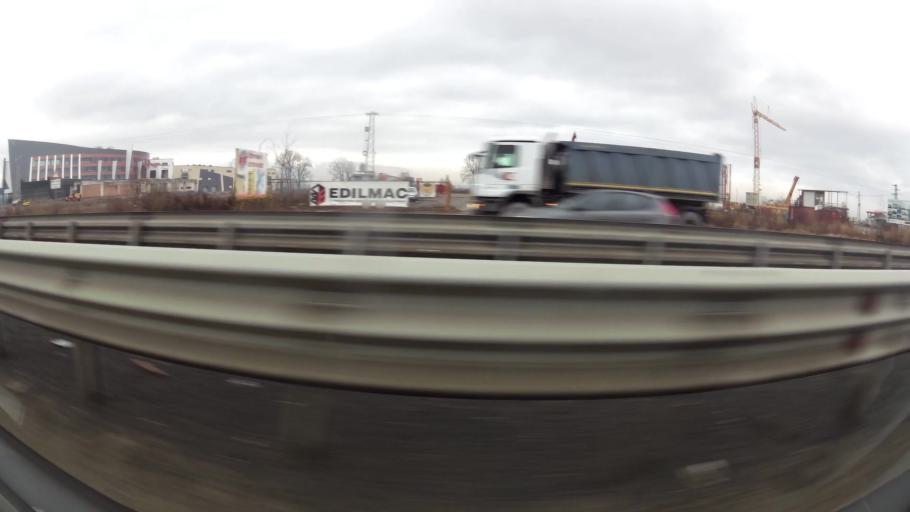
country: BG
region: Sofia-Capital
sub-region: Stolichna Obshtina
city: Sofia
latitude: 42.6815
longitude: 23.4543
